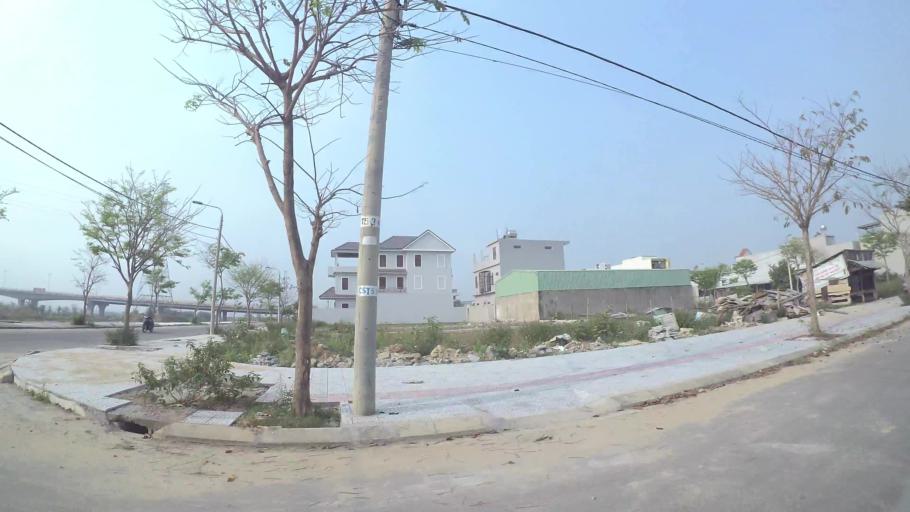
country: VN
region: Da Nang
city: Ngu Hanh Son
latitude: 16.0043
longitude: 108.2285
